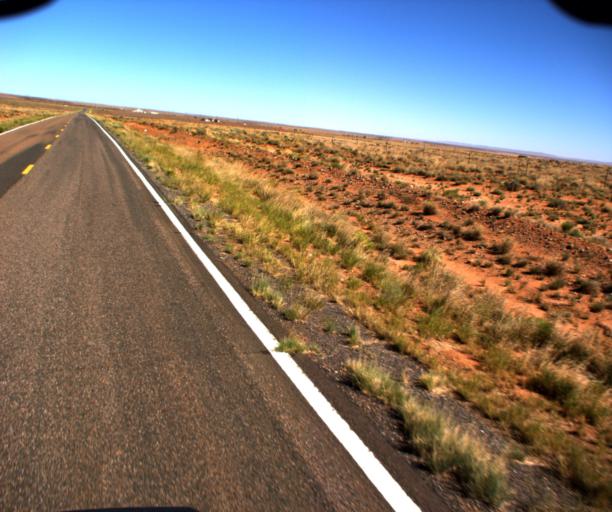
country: US
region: Arizona
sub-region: Coconino County
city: LeChee
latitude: 35.1307
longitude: -110.8796
